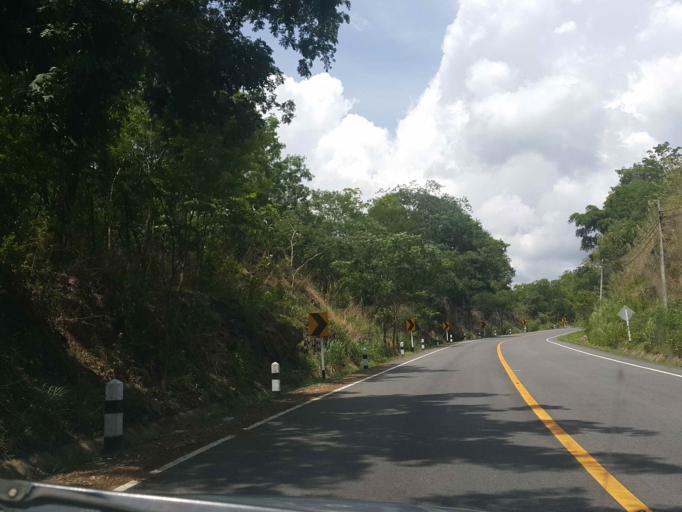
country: TH
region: Phayao
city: Chiang Muan
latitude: 18.8481
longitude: 100.3387
